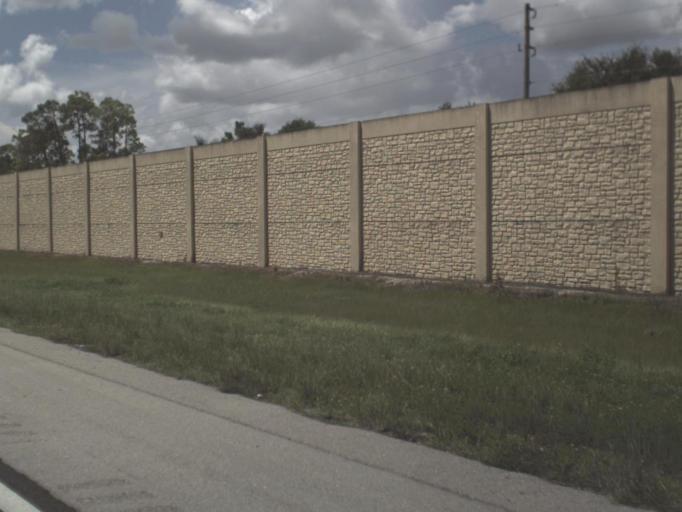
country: US
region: Florida
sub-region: Collier County
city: Golden Gate
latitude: 26.1912
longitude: -81.7359
